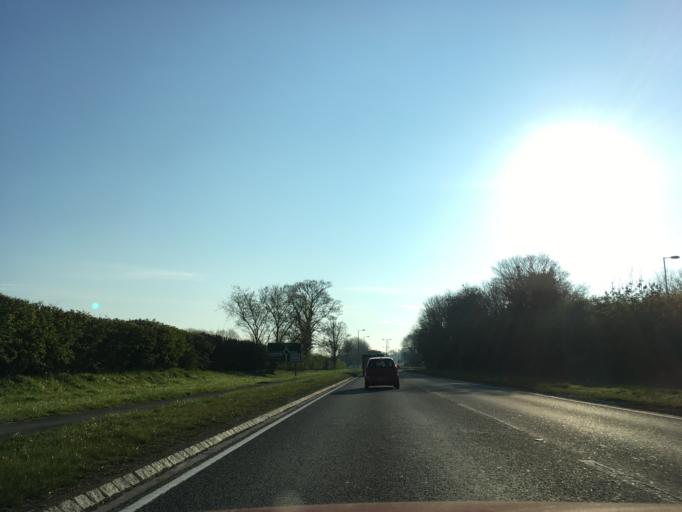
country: GB
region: England
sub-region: Oxfordshire
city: Eynsham
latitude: 51.7878
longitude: -1.3717
